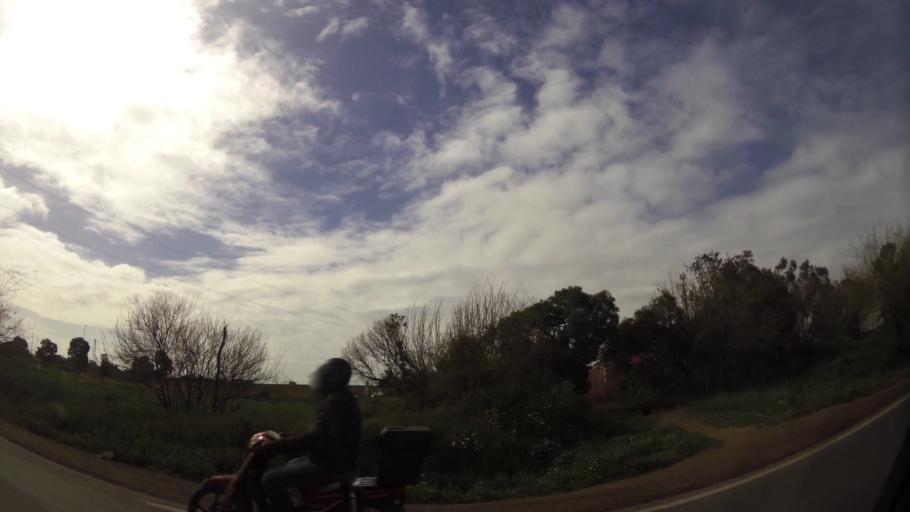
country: MA
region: Grand Casablanca
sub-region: Mohammedia
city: Mohammedia
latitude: 33.6473
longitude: -7.4174
